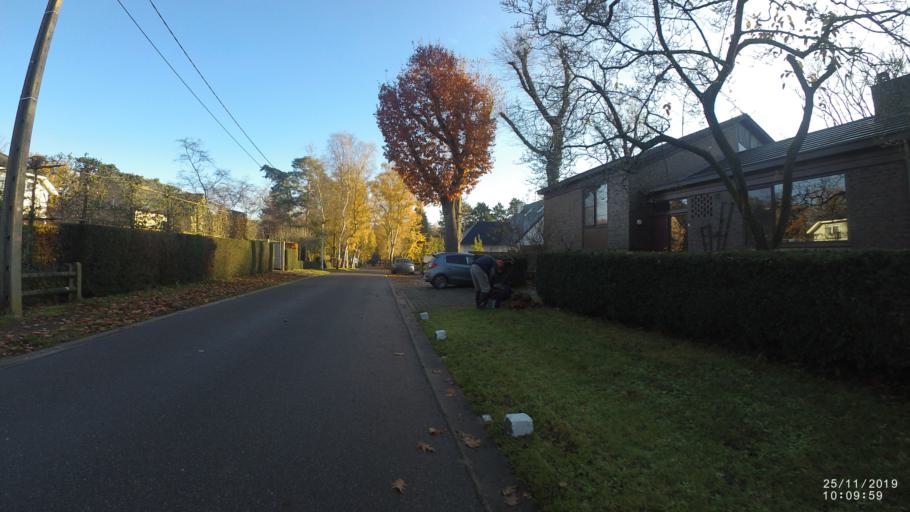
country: BE
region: Flanders
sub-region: Provincie Vlaams-Brabant
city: Diest
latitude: 50.9931
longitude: 5.0207
